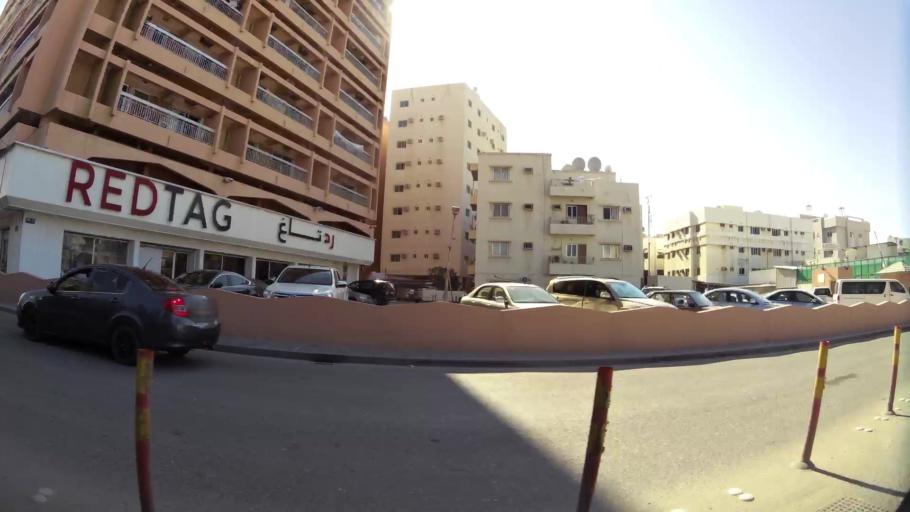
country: BH
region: Manama
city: Manama
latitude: 26.2200
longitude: 50.5738
